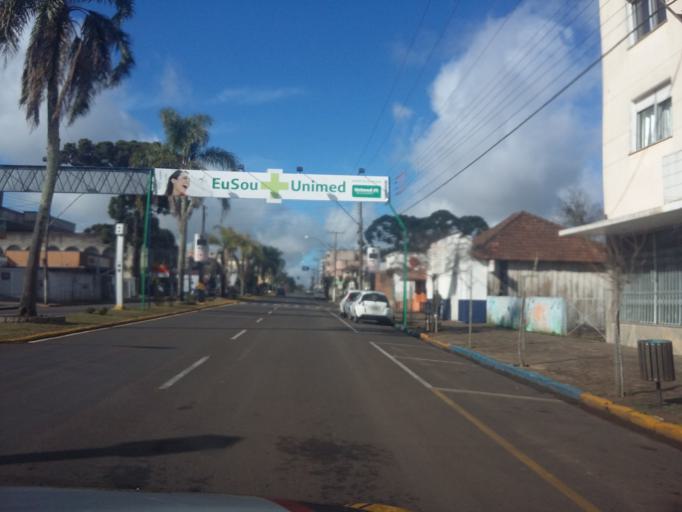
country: BR
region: Rio Grande do Sul
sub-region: Vacaria
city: Vacaria
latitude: -28.5080
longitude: -50.9365
